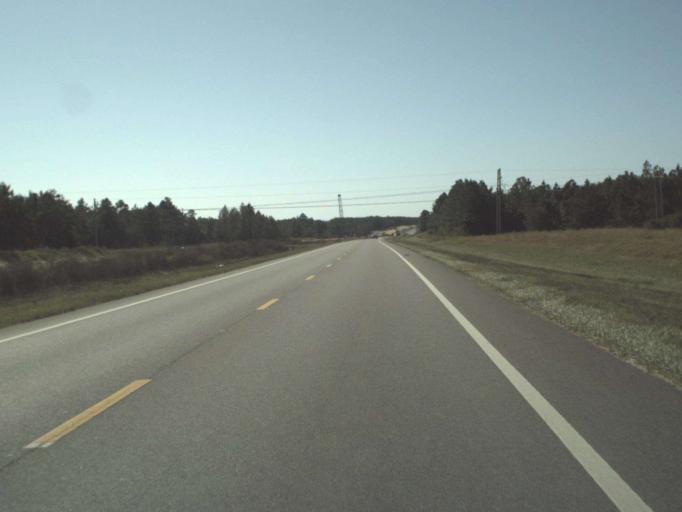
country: US
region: Florida
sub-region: Walton County
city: Freeport
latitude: 30.5327
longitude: -86.1080
